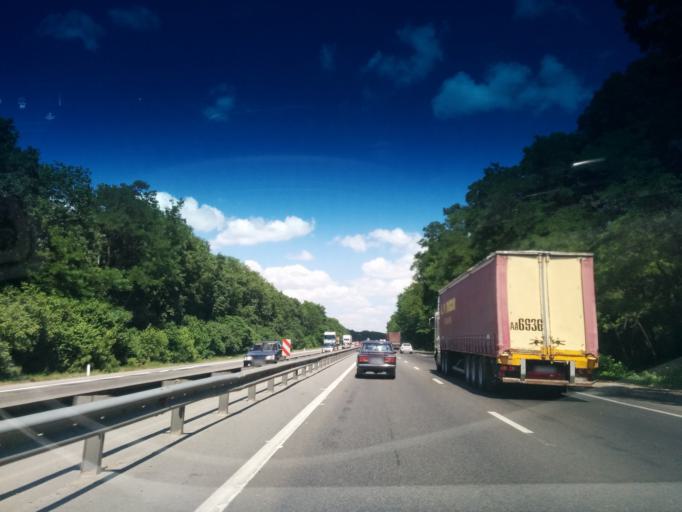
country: RU
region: Rostov
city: Aksay
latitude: 47.3193
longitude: 39.8634
